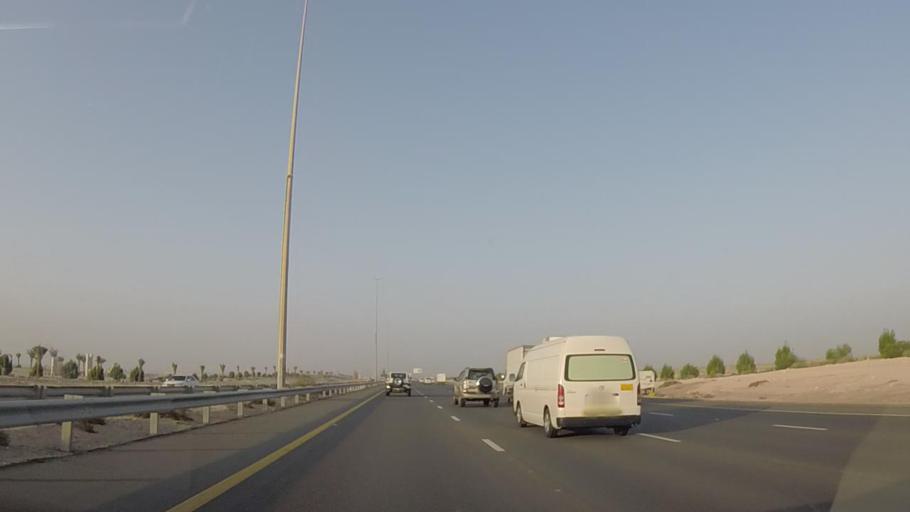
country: AE
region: Dubai
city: Dubai
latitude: 24.9102
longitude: 54.9566
